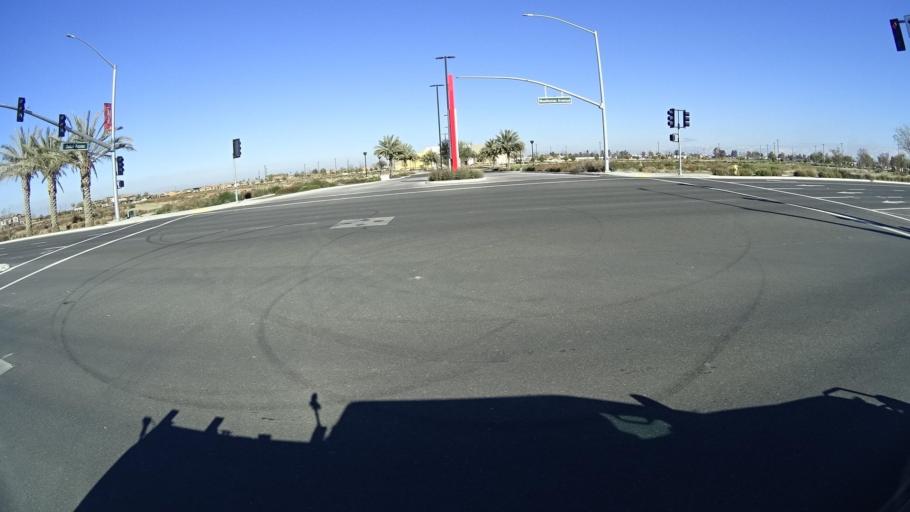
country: US
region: California
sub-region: Kern County
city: Delano
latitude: 35.7468
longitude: -119.2524
